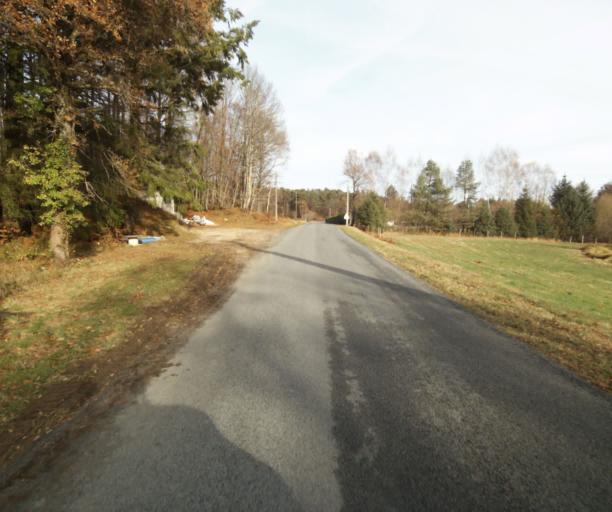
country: FR
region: Limousin
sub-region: Departement de la Correze
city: Sainte-Fortunade
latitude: 45.1765
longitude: 1.7438
